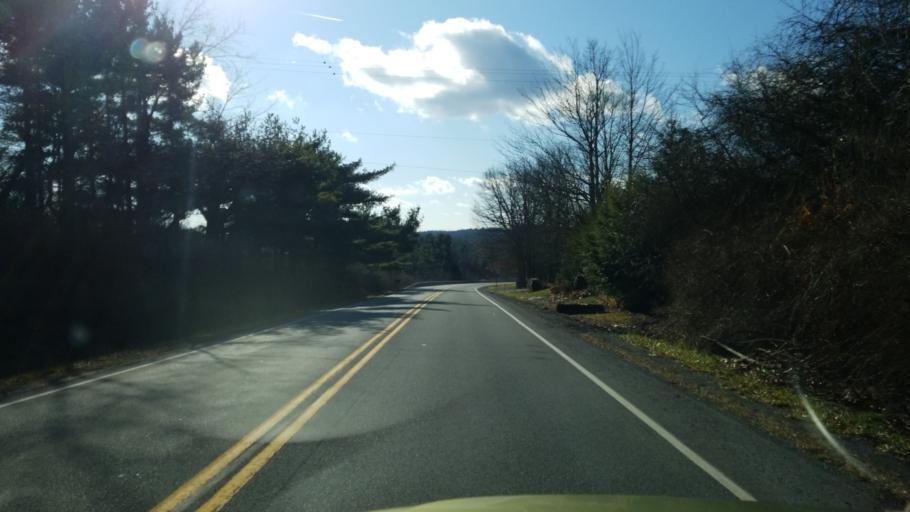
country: US
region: Pennsylvania
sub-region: Clearfield County
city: Hyde
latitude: 40.9912
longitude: -78.4420
